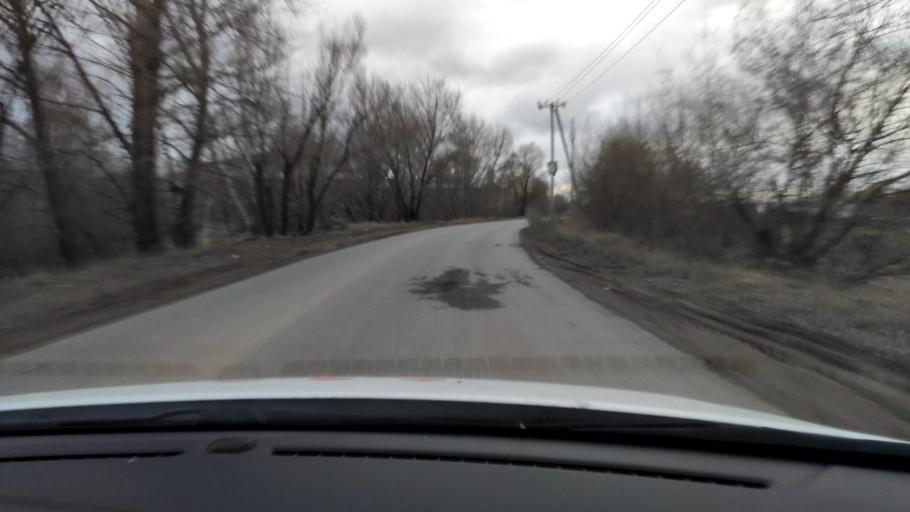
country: RU
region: Tatarstan
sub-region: Gorod Kazan'
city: Kazan
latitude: 55.7233
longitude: 49.0948
